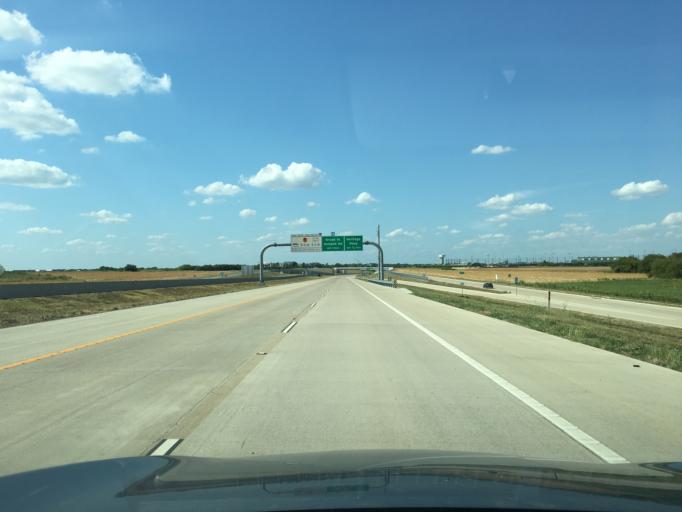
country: US
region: Texas
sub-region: Tarrant County
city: Mansfield
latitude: 32.5468
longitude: -97.0836
